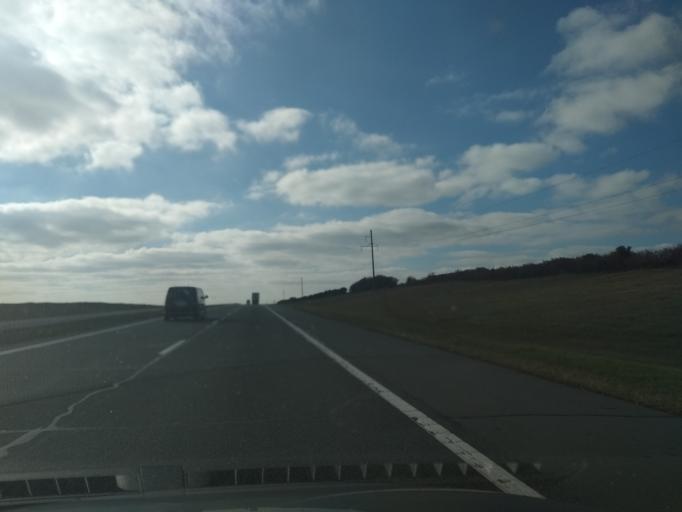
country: BY
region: Minsk
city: Novy Svyerzhan'
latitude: 53.4698
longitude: 26.6172
